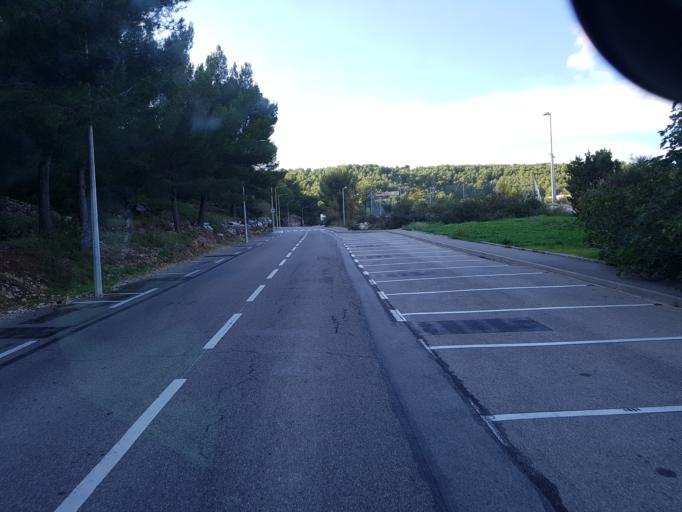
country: FR
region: Provence-Alpes-Cote d'Azur
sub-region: Departement des Bouches-du-Rhone
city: Cassis
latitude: 43.2291
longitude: 5.5354
